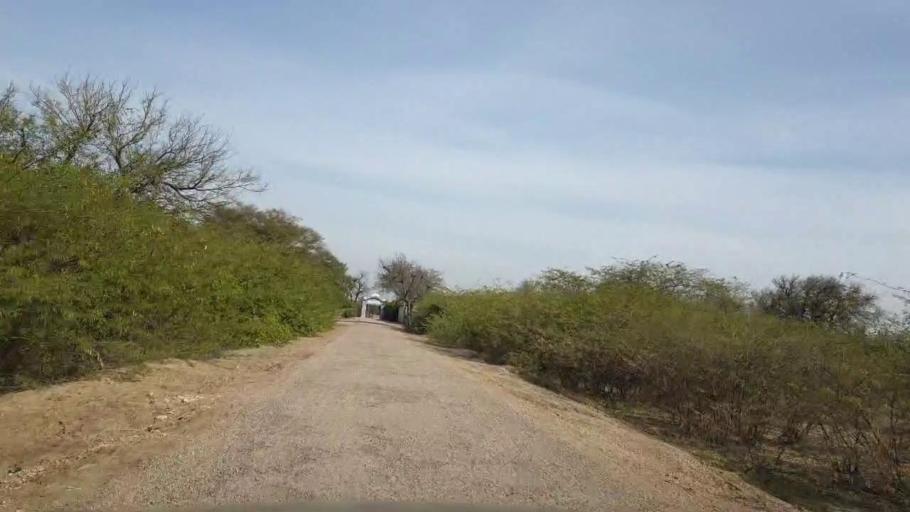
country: PK
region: Sindh
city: Kunri
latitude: 25.1576
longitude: 69.6554
